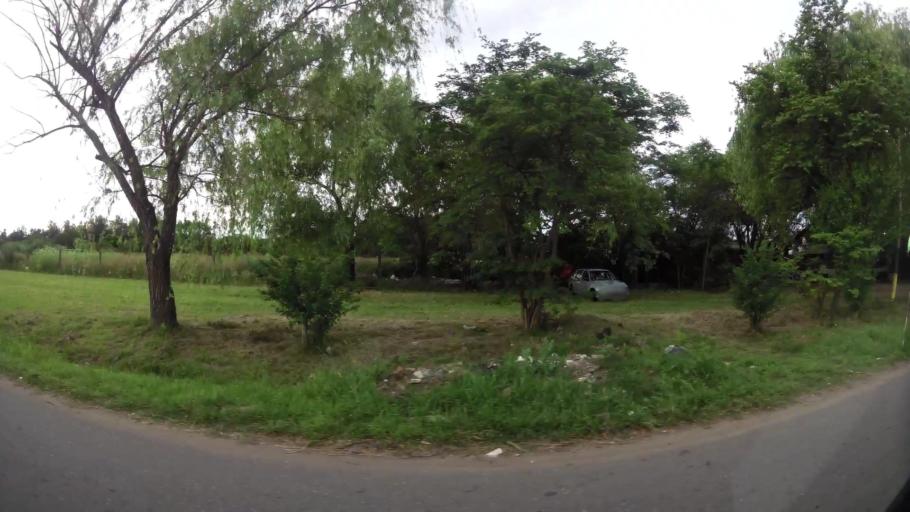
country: AR
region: Santa Fe
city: Gobernador Galvez
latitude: -32.9981
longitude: -60.6814
